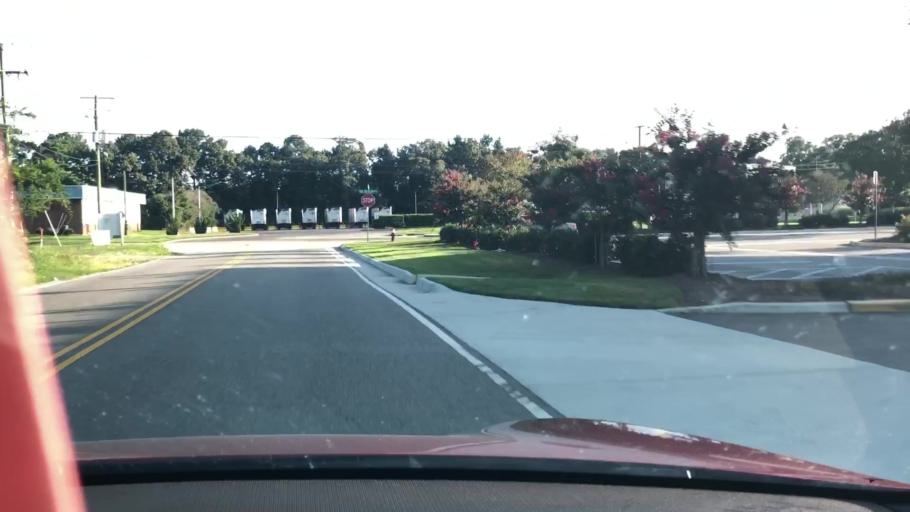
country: US
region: Virginia
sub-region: City of Virginia Beach
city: Virginia Beach
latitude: 36.8447
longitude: -76.0354
